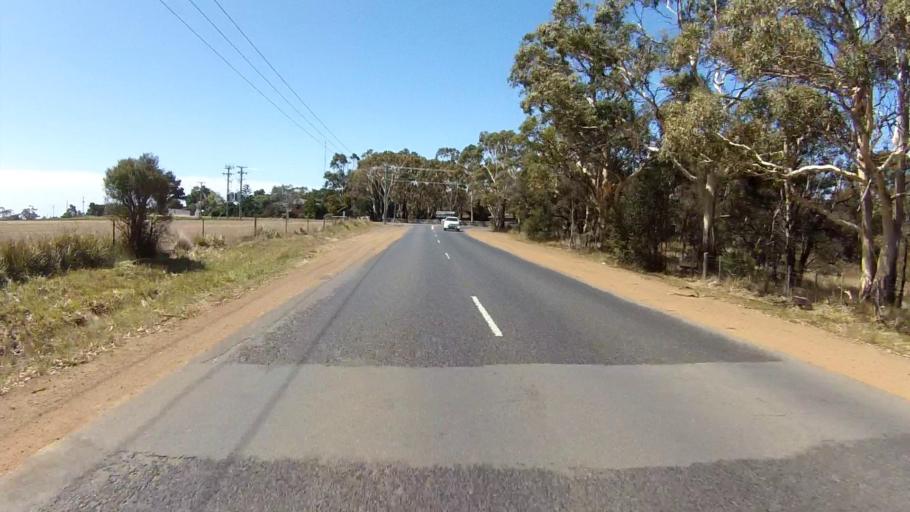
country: AU
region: Tasmania
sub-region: Clarence
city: Sandford
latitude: -42.9362
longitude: 147.4916
